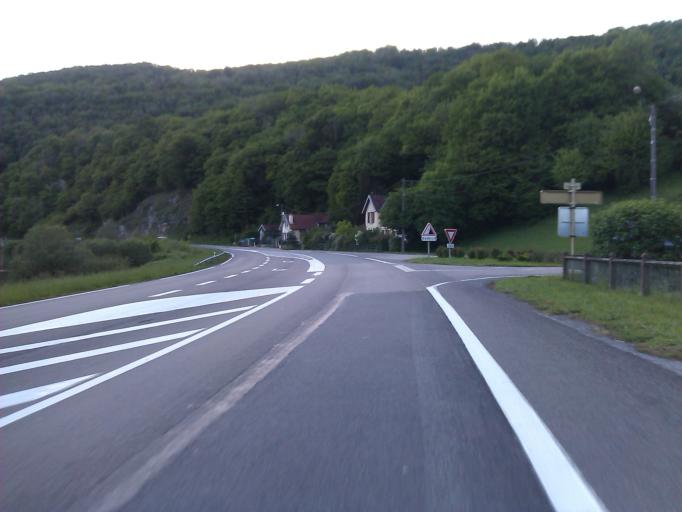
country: FR
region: Franche-Comte
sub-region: Departement du Doubs
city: Baume-les-Dames
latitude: 47.3723
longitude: 6.4276
